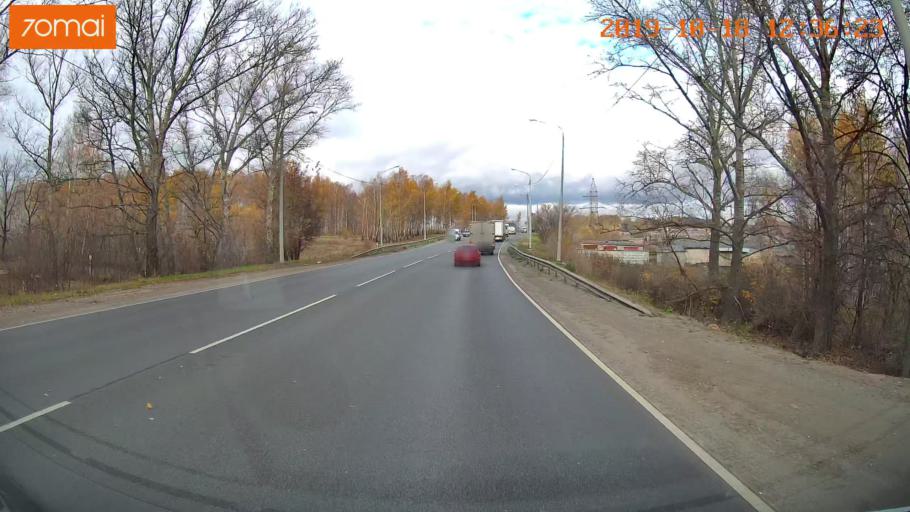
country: RU
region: Rjazan
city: Ryazan'
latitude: 54.6341
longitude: 39.6335
